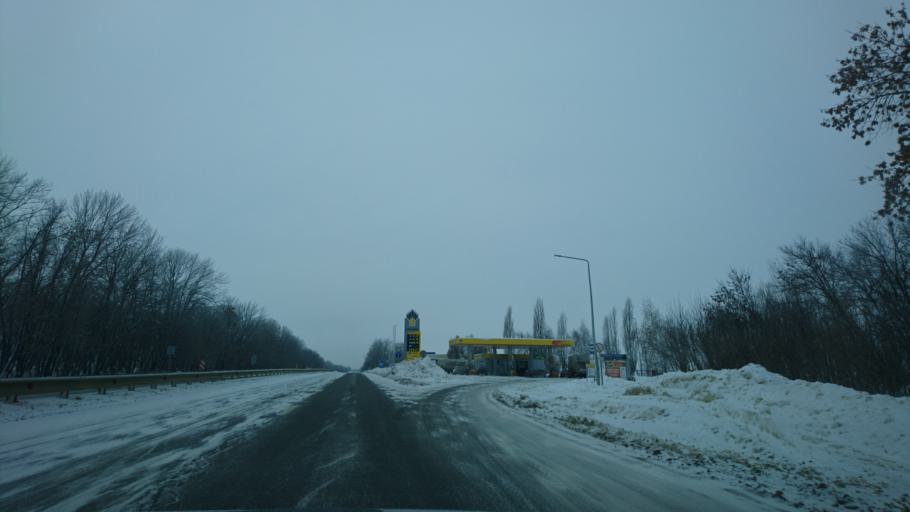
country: RU
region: Belgorod
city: Mayskiy
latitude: 50.4359
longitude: 36.3899
